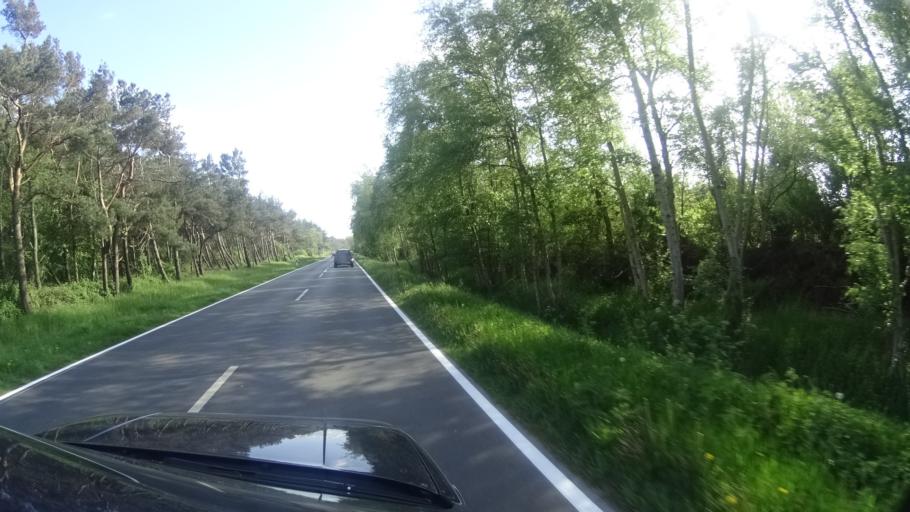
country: DE
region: Mecklenburg-Vorpommern
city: Ostseebad Dierhagen
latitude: 54.3311
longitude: 12.3739
